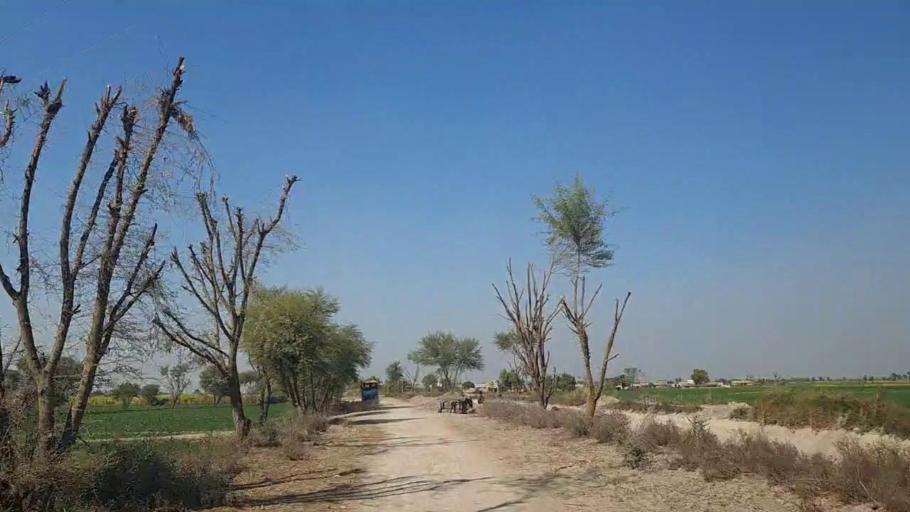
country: PK
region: Sindh
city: Sakrand
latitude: 26.2719
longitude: 68.2206
